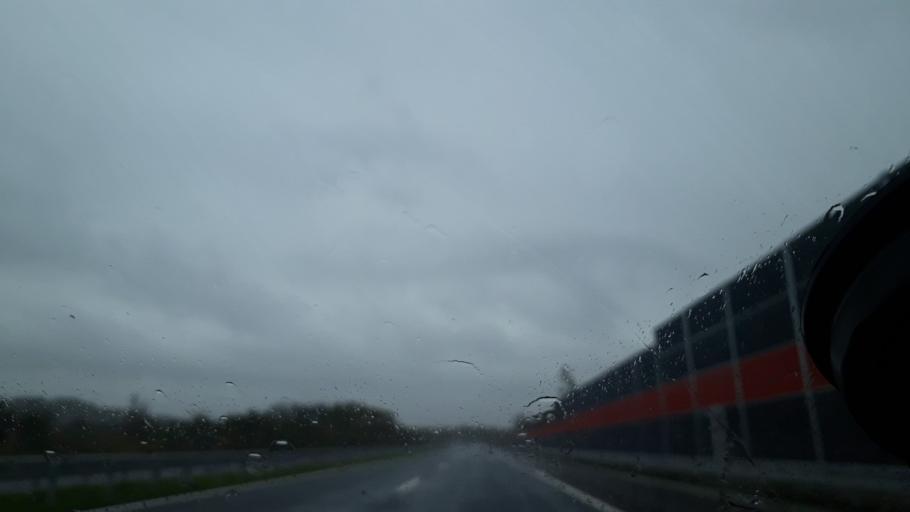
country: BA
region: Republika Srpska
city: Maglajani
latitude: 44.8832
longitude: 17.3798
